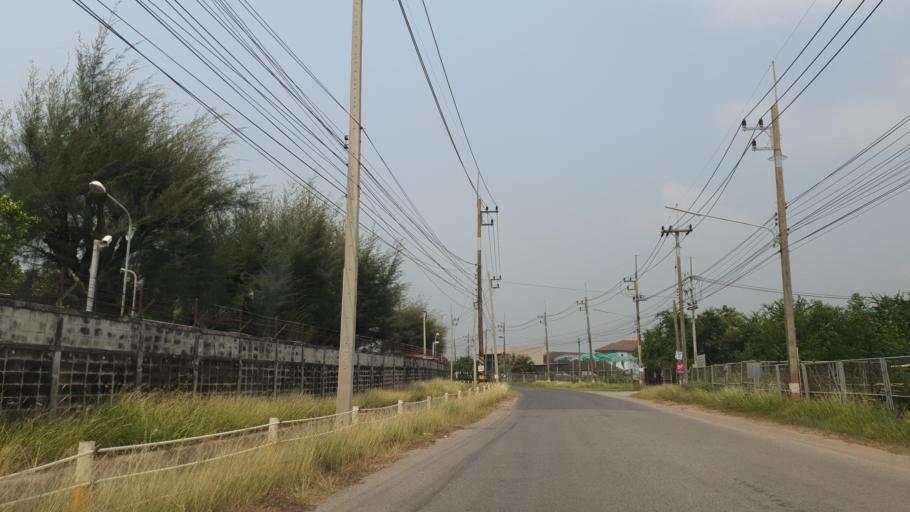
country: TH
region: Chachoengsao
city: Bang Pakong
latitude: 13.4990
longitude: 101.0319
